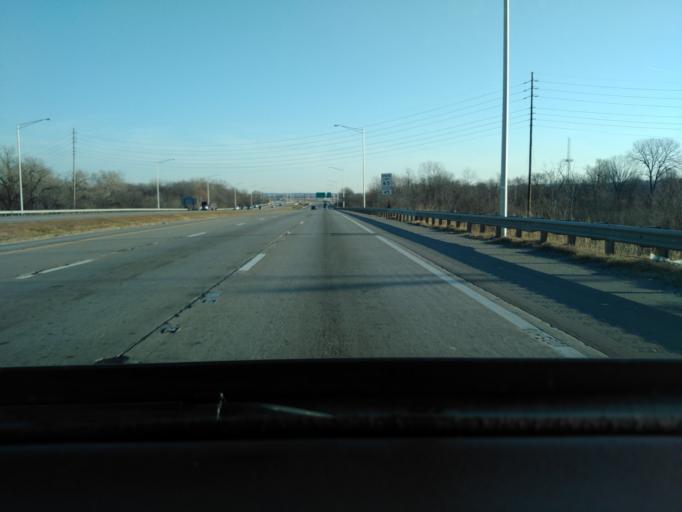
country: US
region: Illinois
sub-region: Saint Clair County
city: Washington Park
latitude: 38.6099
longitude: -90.0798
